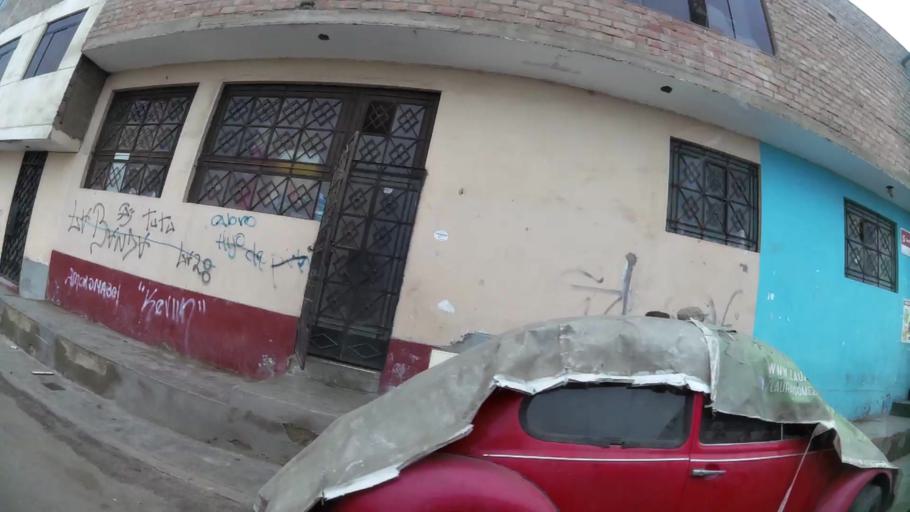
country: PE
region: Lima
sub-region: Lima
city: Surco
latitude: -12.1694
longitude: -76.9591
